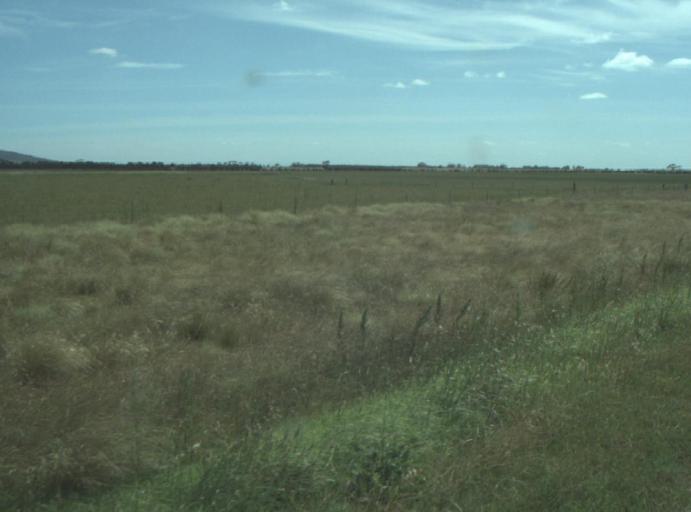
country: AU
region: Victoria
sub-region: Greater Geelong
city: Lara
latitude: -38.0105
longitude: 144.4581
